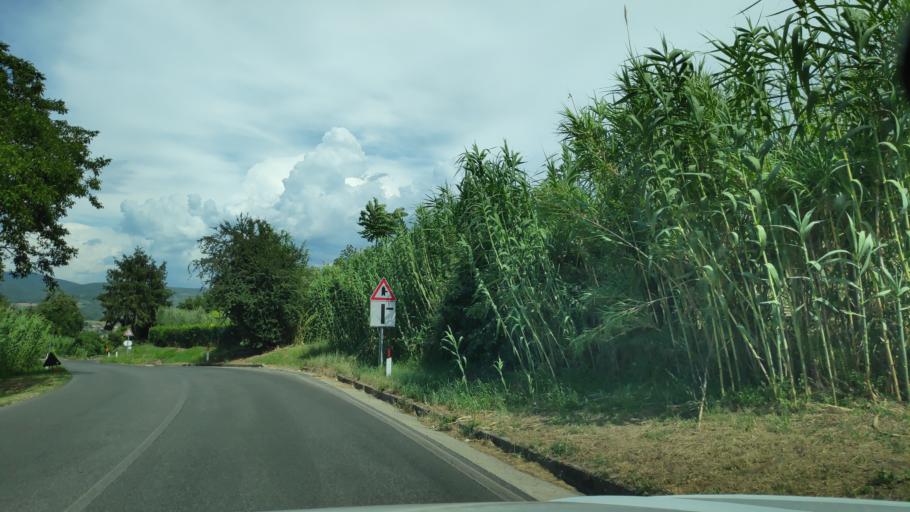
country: IT
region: Umbria
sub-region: Provincia di Terni
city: Orvieto
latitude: 42.7257
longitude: 12.1160
